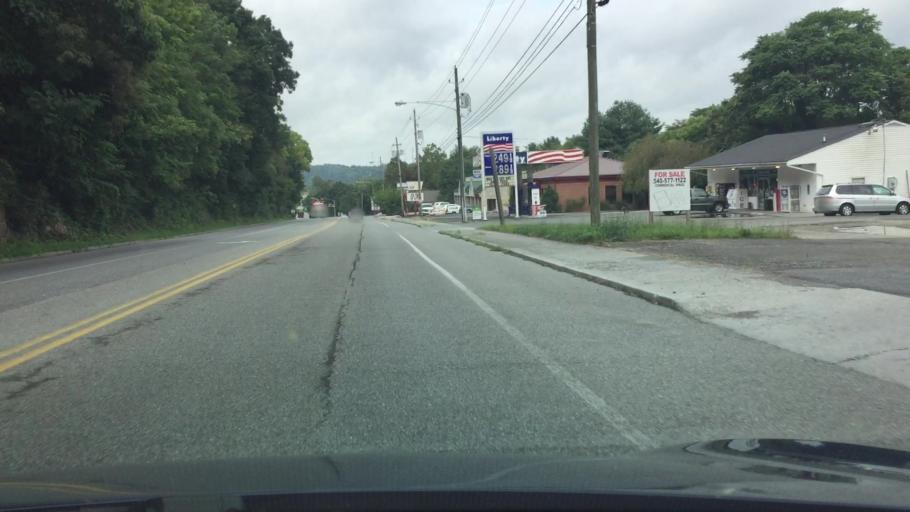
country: US
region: Virginia
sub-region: City of Radford
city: Radford
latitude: 37.1400
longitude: -80.5630
